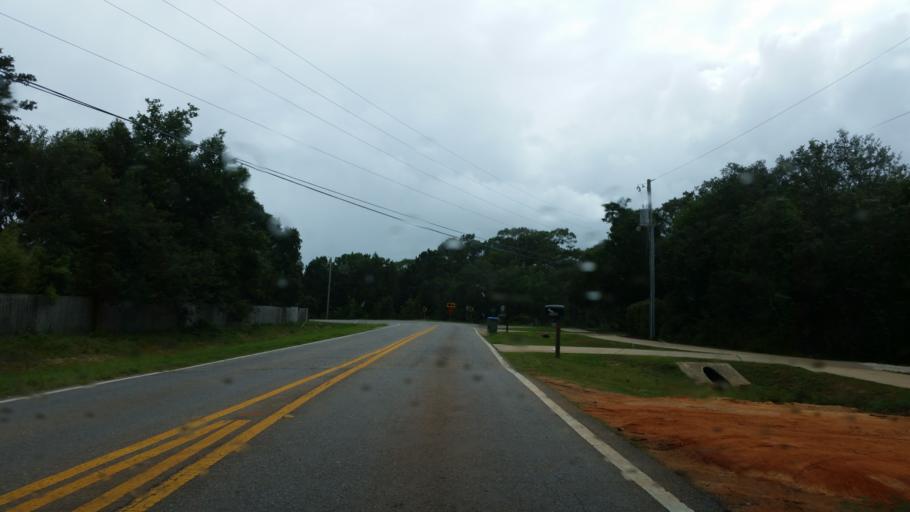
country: US
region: Florida
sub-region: Santa Rosa County
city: Woodlawn Beach
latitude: 30.4087
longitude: -86.9989
